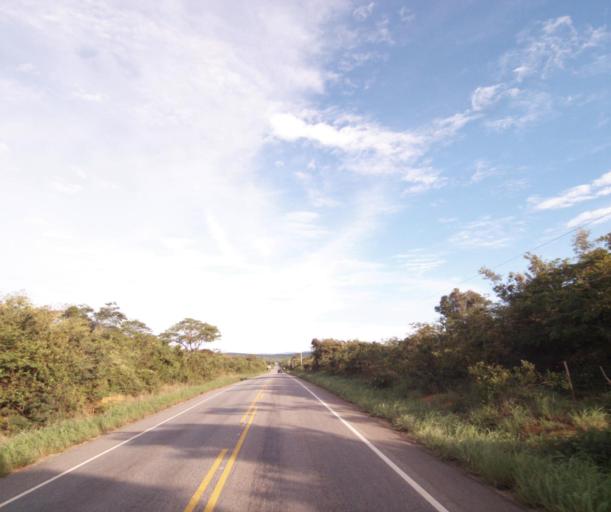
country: BR
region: Bahia
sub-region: Caetite
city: Caetite
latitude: -14.1201
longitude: -42.4267
